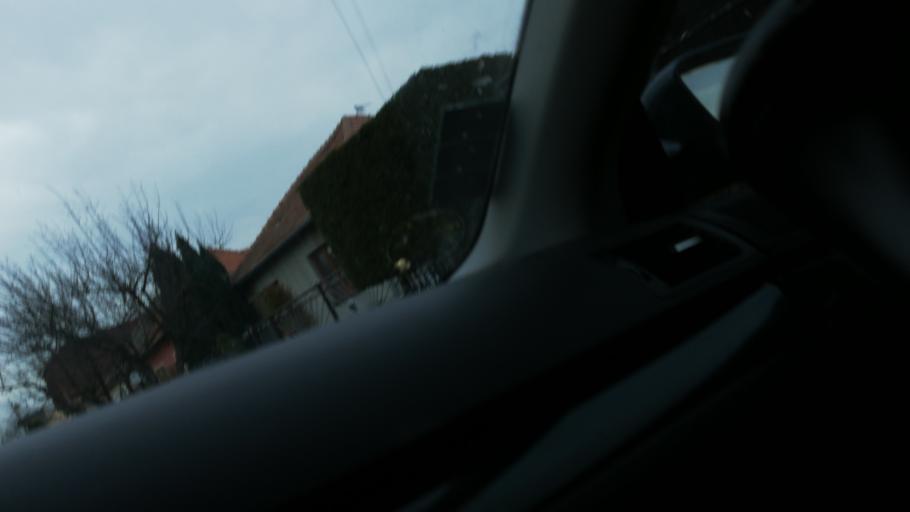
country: SK
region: Nitriansky
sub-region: Okres Nitra
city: Nitra
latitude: 48.3191
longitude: 17.9882
